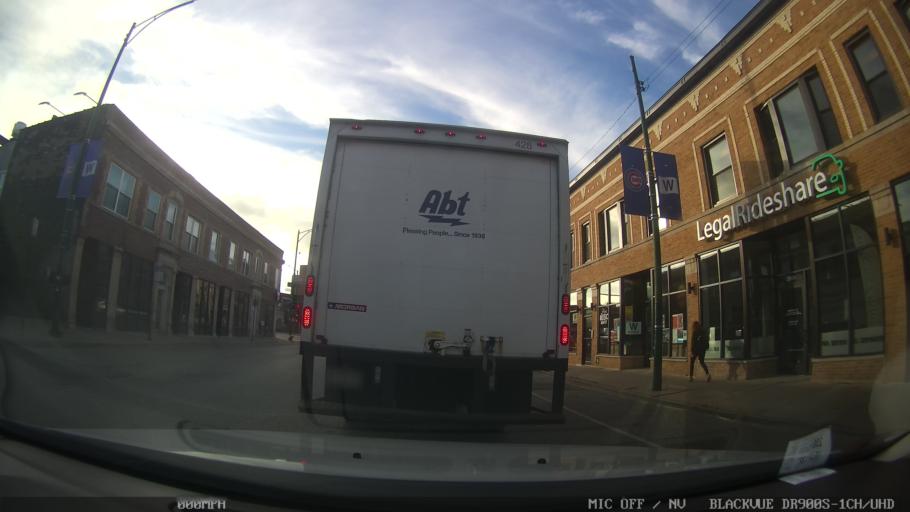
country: US
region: Illinois
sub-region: Cook County
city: Lincolnwood
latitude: 41.9514
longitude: -87.6599
